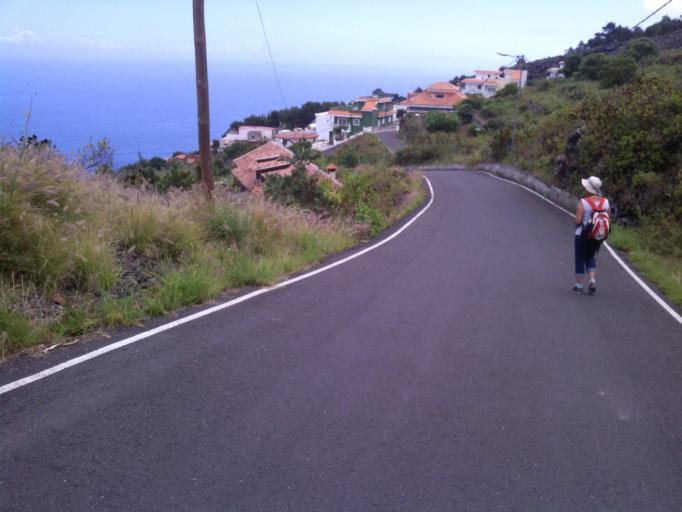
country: ES
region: Canary Islands
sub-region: Provincia de Santa Cruz de Tenerife
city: Garachico
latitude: 28.3618
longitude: -16.7713
